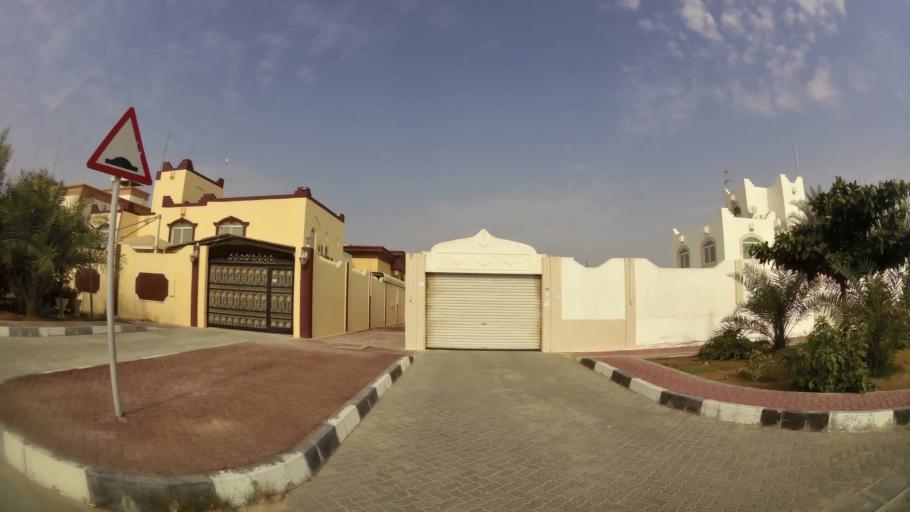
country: AE
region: Abu Dhabi
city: Abu Dhabi
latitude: 24.6602
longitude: 54.7695
